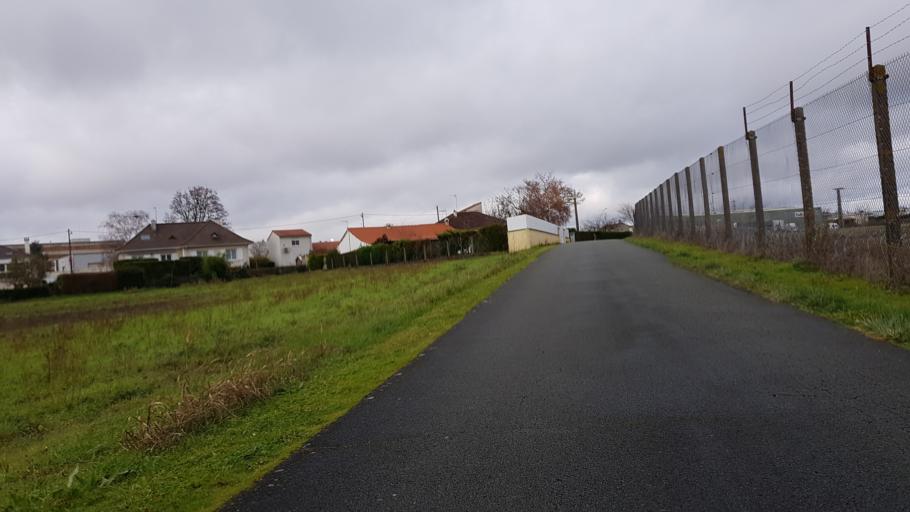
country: FR
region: Poitou-Charentes
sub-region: Departement de la Vienne
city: Chasseneuil-du-Poitou
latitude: 46.6540
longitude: 0.3734
